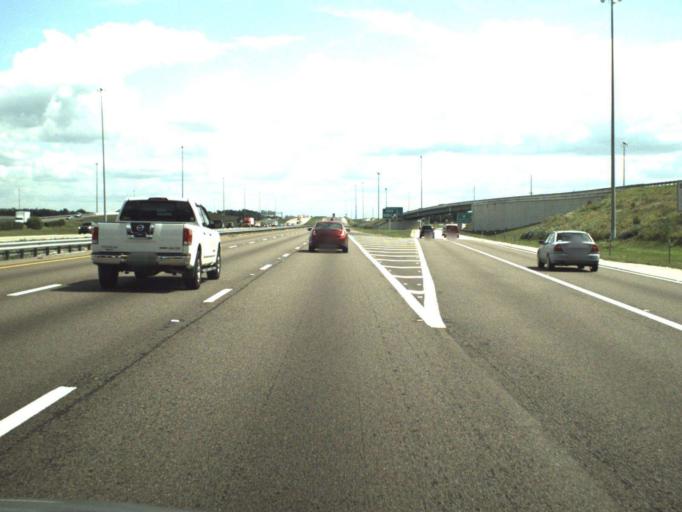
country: US
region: Florida
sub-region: Seminole County
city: Heathrow
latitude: 28.7866
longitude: -81.3502
